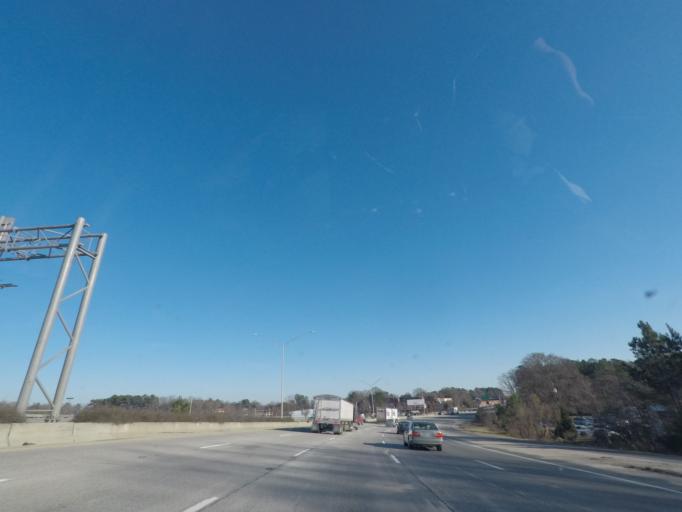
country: US
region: North Carolina
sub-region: Durham County
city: Durham
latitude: 36.0283
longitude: -78.9218
